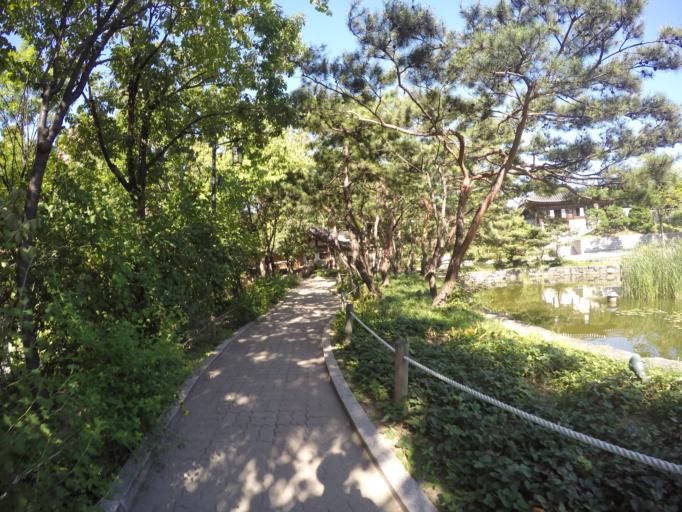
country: KR
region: Seoul
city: Seoul
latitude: 37.5596
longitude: 126.9937
